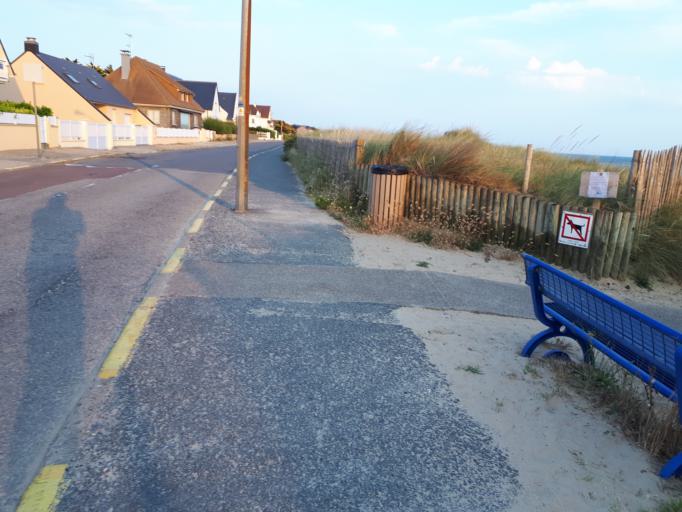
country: FR
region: Lower Normandy
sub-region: Departement de la Manche
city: Barneville-Plage
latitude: 49.3634
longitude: -1.7645
